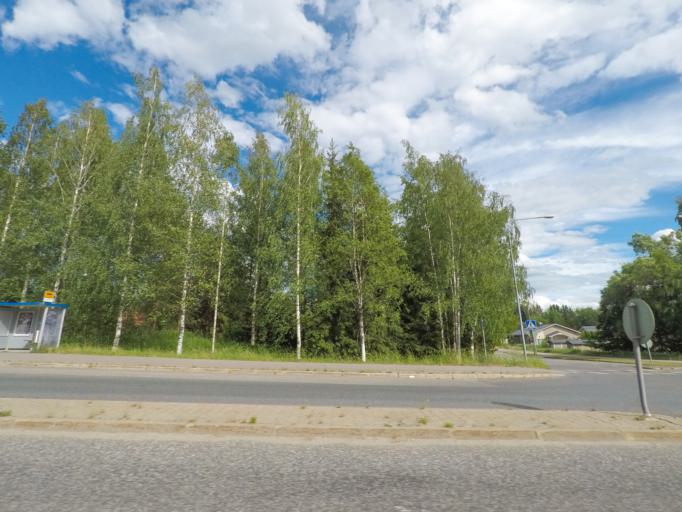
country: FI
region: Paijanne Tavastia
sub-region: Lahti
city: Lahti
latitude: 60.9616
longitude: 25.6225
